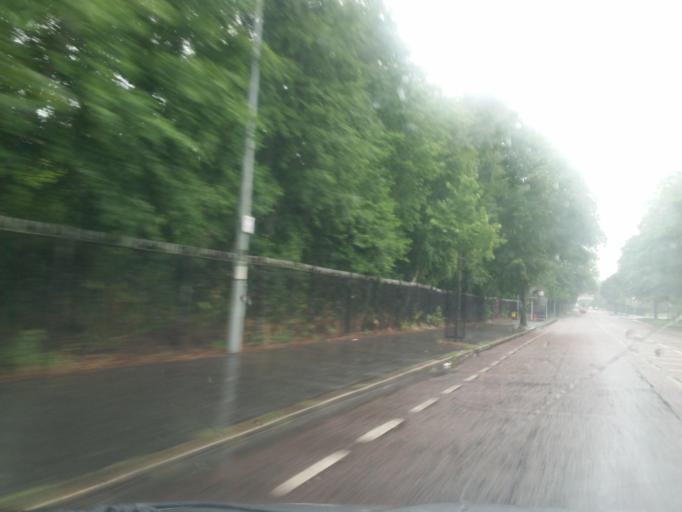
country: GB
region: Northern Ireland
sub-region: Castlereagh District
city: Castlereagh
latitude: 54.6105
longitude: -5.8660
